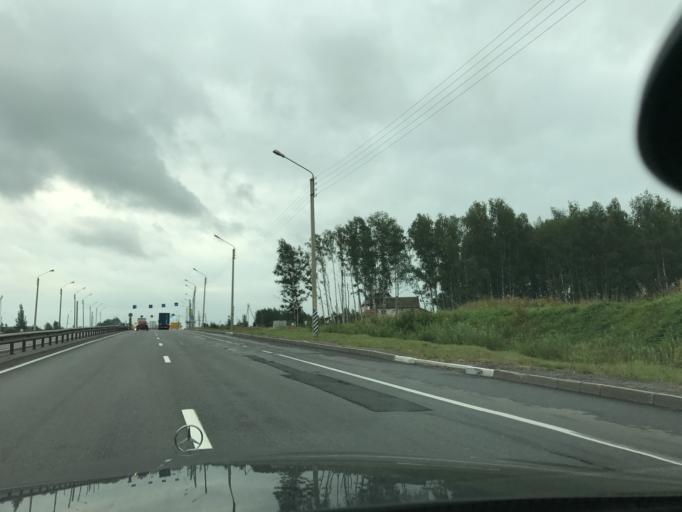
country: RU
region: Vladimir
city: Novovyazniki
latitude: 56.2197
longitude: 42.1786
